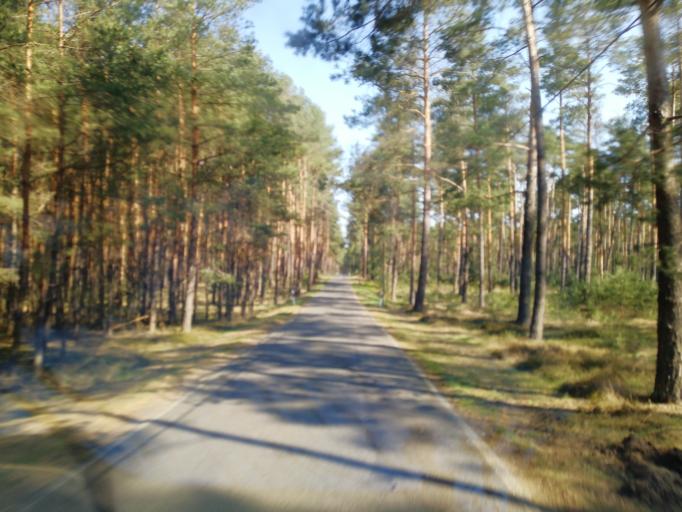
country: DE
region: Brandenburg
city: Bronkow
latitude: 51.6768
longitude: 13.8641
